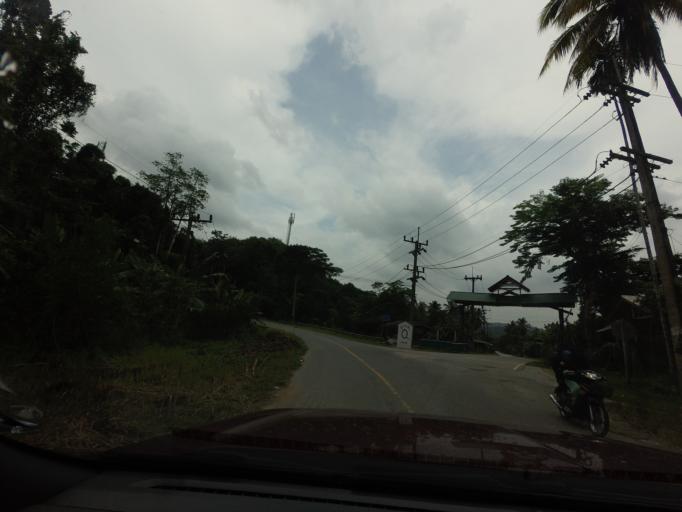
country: TH
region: Yala
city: Than To
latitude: 6.1998
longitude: 101.2371
